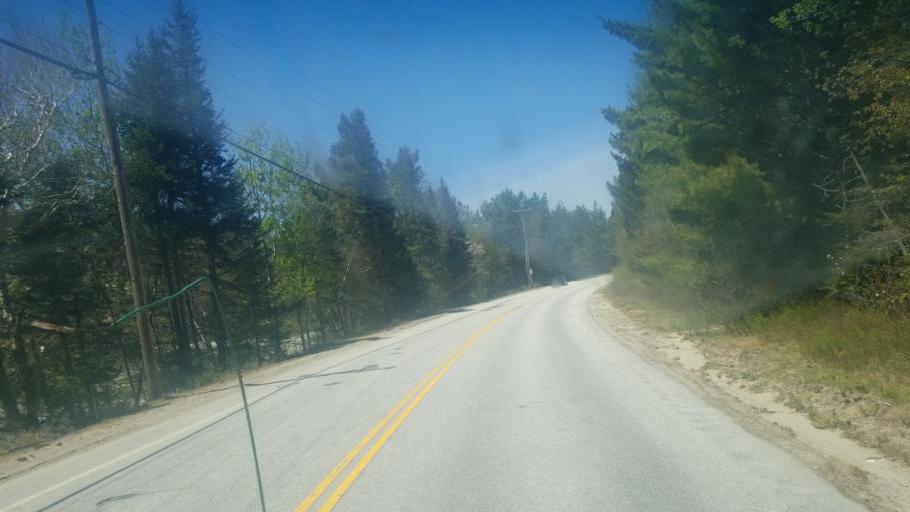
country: US
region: New Hampshire
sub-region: Coos County
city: Jefferson
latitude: 44.2596
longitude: -71.4495
